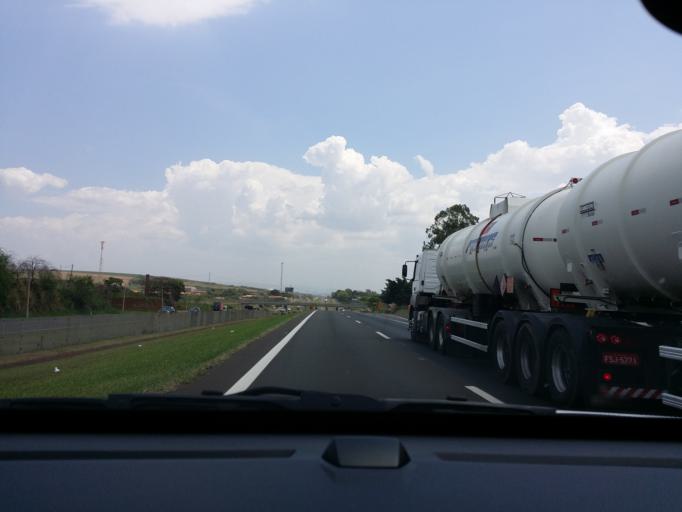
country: BR
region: Sao Paulo
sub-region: Cordeiropolis
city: Cordeiropolis
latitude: -22.4819
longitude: -47.4682
